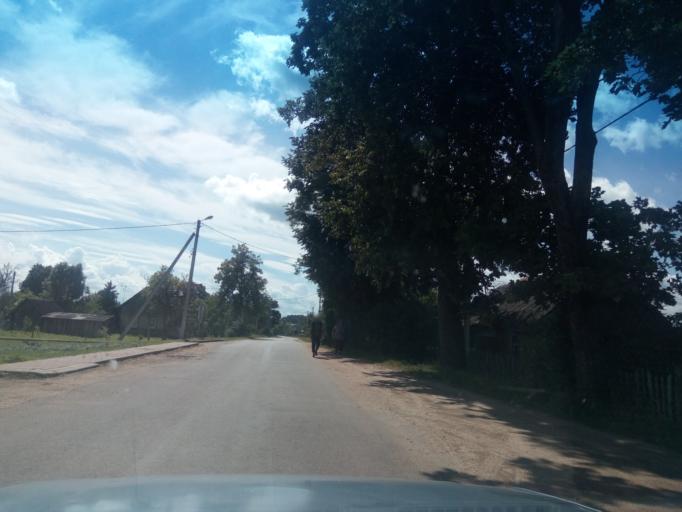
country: BY
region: Vitebsk
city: Dzisna
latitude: 55.6679
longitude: 28.3282
